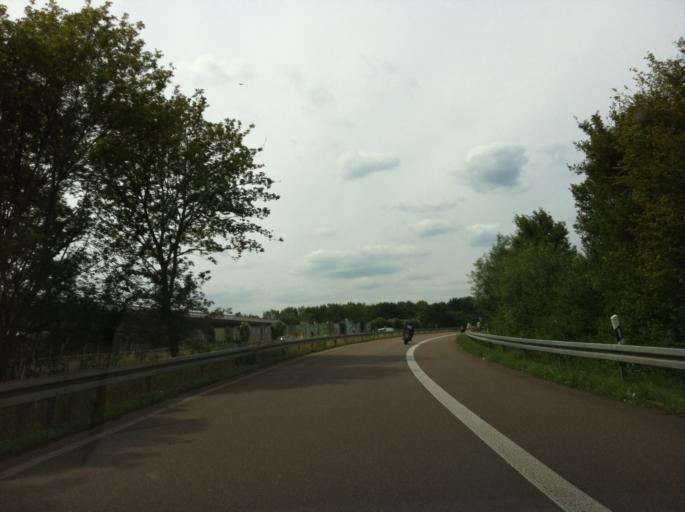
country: DE
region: Hesse
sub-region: Regierungsbezirk Darmstadt
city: Hattersheim
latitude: 50.0828
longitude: 8.4904
